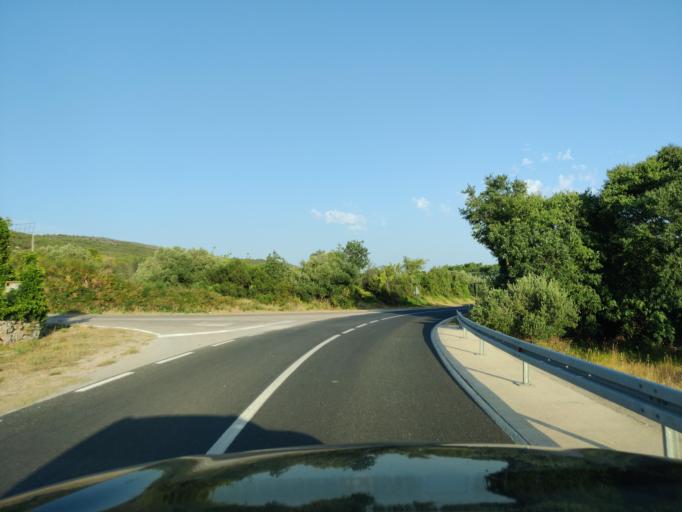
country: HR
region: Sibensko-Kniniska
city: Tribunj
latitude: 43.7717
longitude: 15.7265
